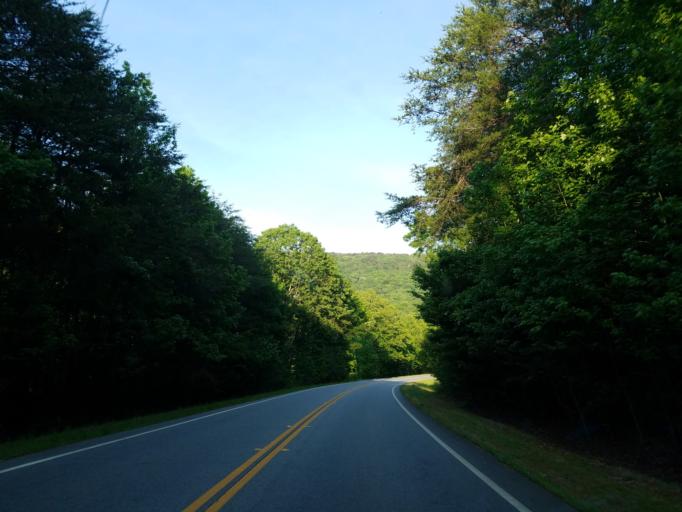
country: US
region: Georgia
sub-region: Whitfield County
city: Dalton
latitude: 34.6762
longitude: -85.0674
